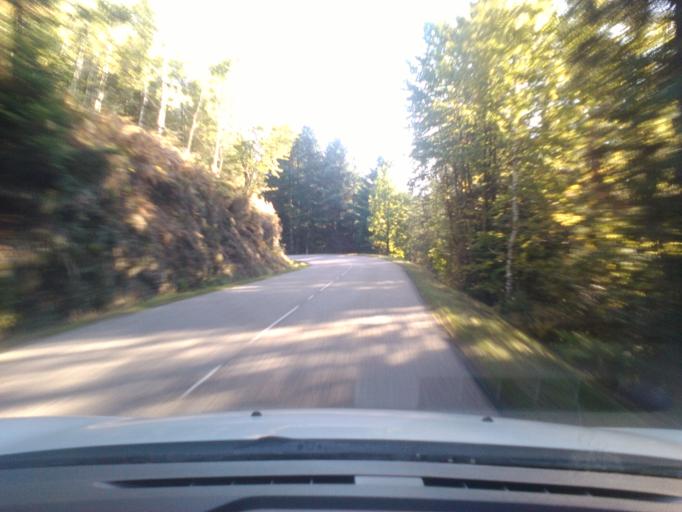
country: FR
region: Lorraine
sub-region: Departement des Vosges
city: Etival-Clairefontaine
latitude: 48.2949
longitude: 6.7846
